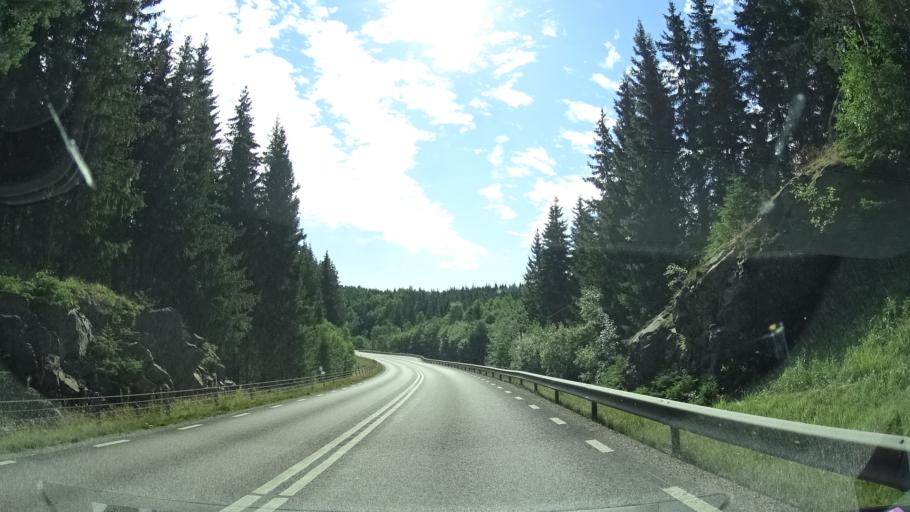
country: SE
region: Vaermland
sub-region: Arjangs Kommun
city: Toecksfors
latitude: 59.4970
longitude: 11.8851
